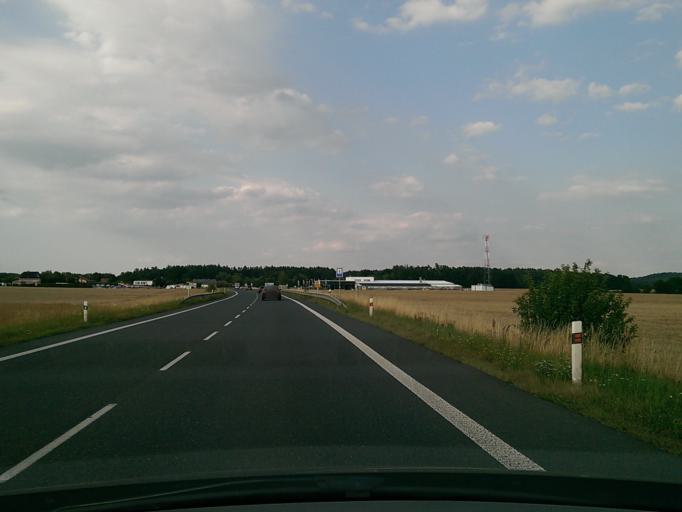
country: CZ
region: Central Bohemia
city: Knezmost
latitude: 50.4289
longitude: 15.0354
